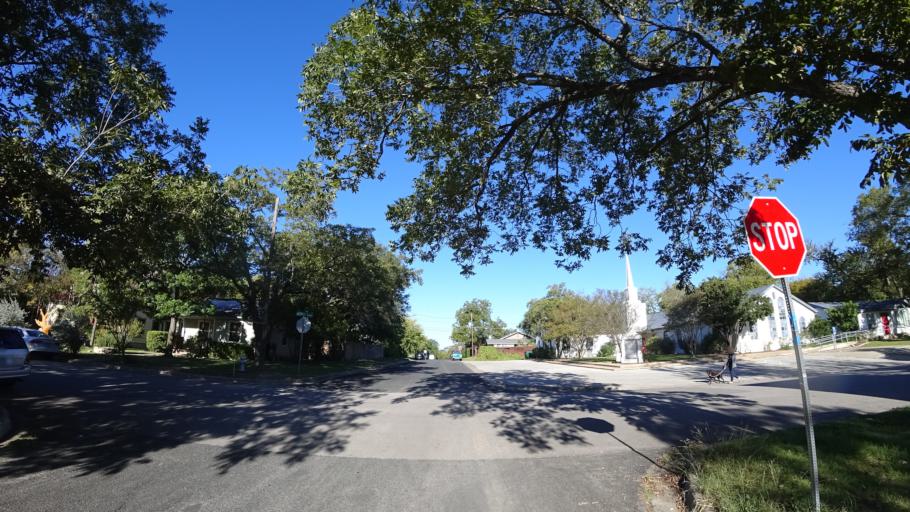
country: US
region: Texas
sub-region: Travis County
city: Austin
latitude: 30.3194
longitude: -97.7188
